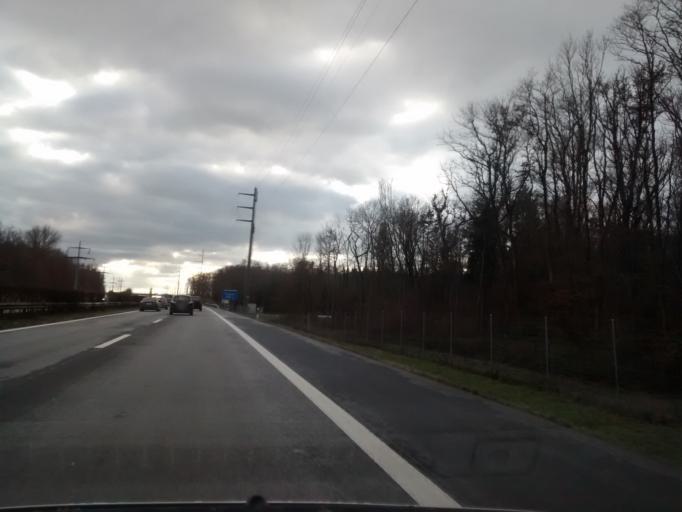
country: CH
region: Vaud
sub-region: Nyon District
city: Founex
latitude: 46.3535
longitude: 6.1748
